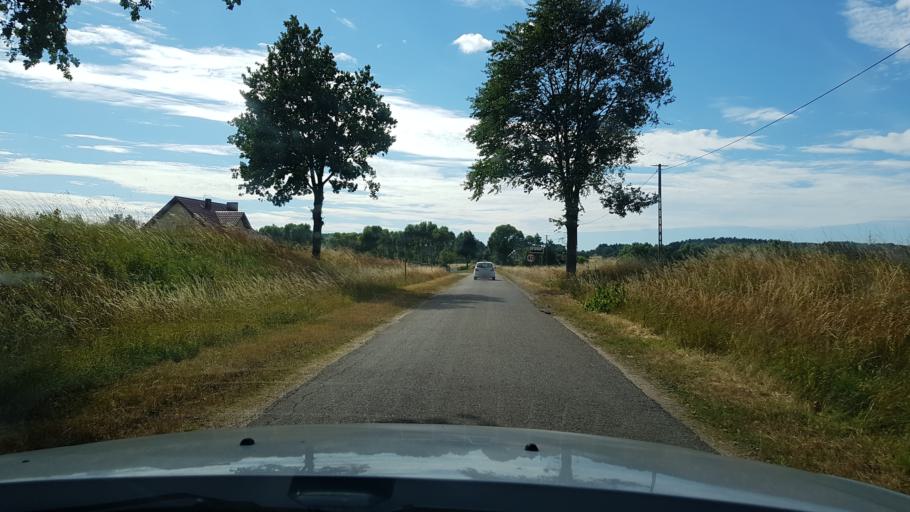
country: PL
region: West Pomeranian Voivodeship
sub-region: Powiat drawski
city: Zlocieniec
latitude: 53.6328
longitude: 16.0528
